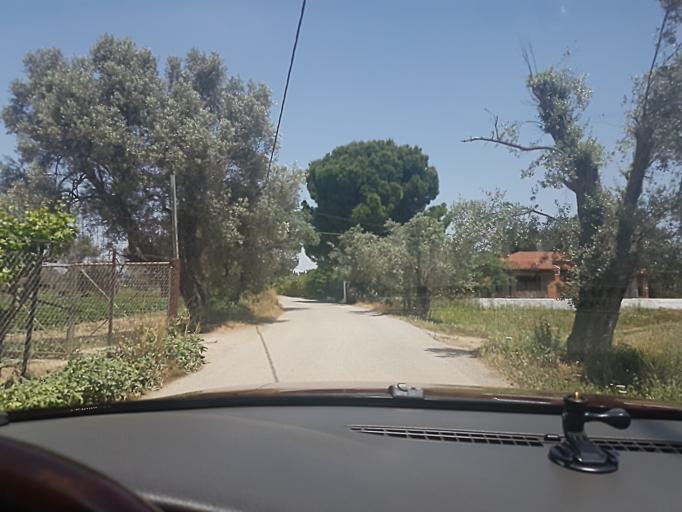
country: GR
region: Central Greece
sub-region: Nomos Evvoias
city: Vasilikon
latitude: 38.4103
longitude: 23.6663
